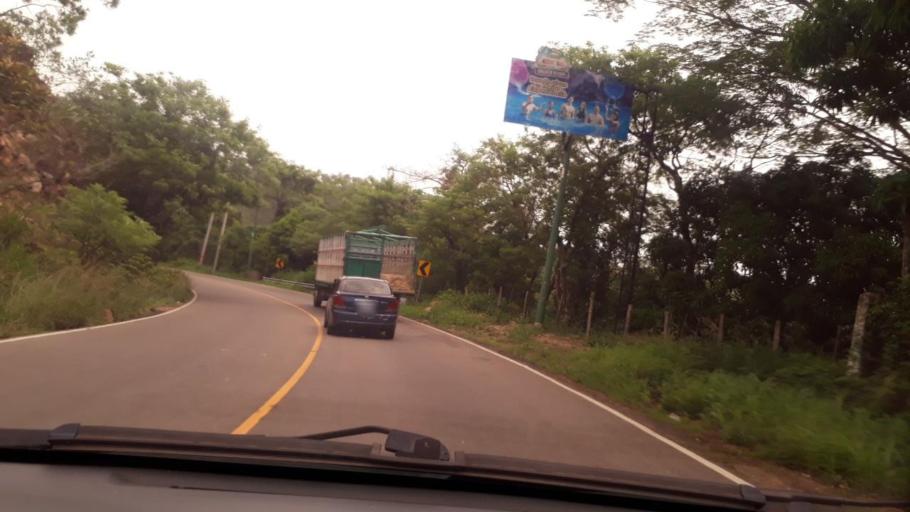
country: GT
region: Chiquimula
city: Concepcion Las Minas
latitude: 14.5635
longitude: -89.4532
